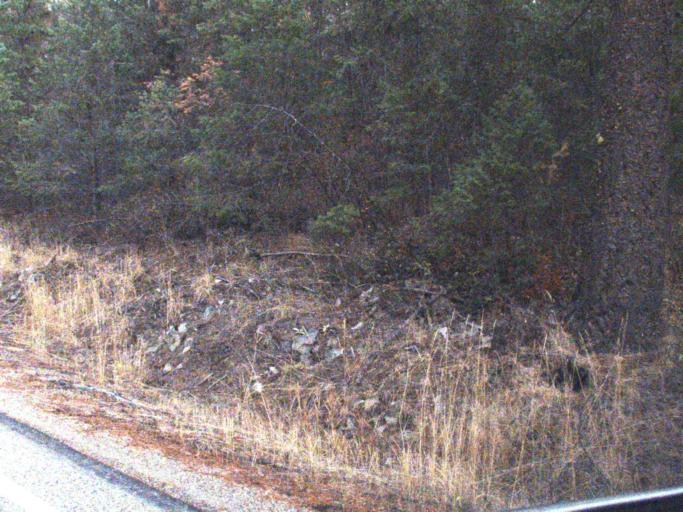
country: CA
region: British Columbia
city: Grand Forks
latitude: 48.9146
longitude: -118.2068
